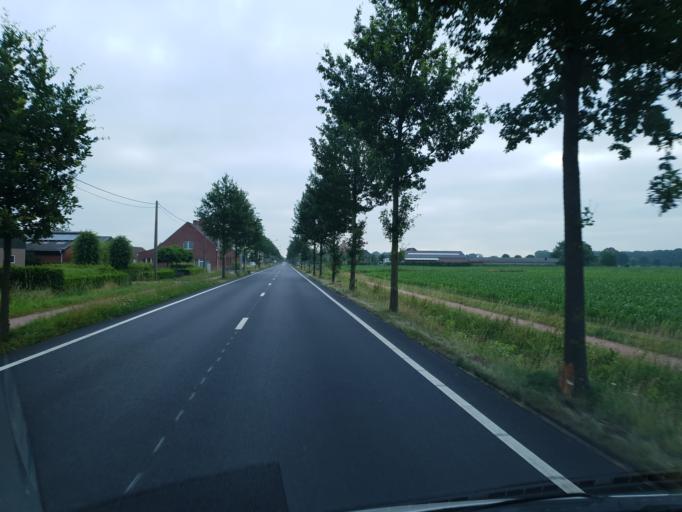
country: BE
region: Flanders
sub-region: Provincie Antwerpen
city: Hoogstraten
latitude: 51.3748
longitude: 4.7173
